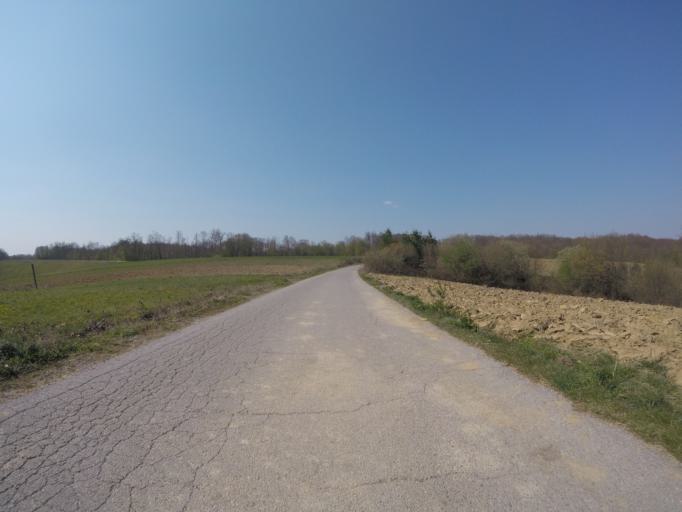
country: HR
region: Grad Zagreb
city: Strmec
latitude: 45.5609
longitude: 15.9067
